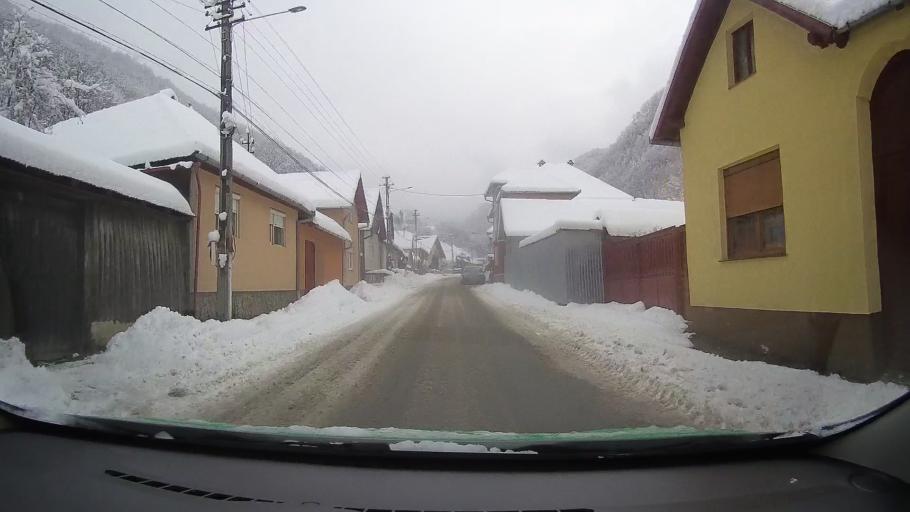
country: RO
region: Alba
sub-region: Comuna Sugag
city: Dobra
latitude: 45.7595
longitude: 23.6615
